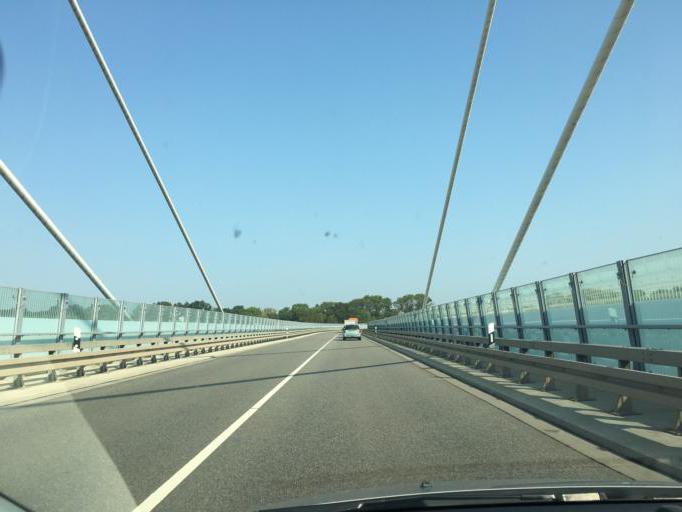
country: DE
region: Saxony-Anhalt
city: Schonebeck
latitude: 52.0234
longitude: 11.7581
